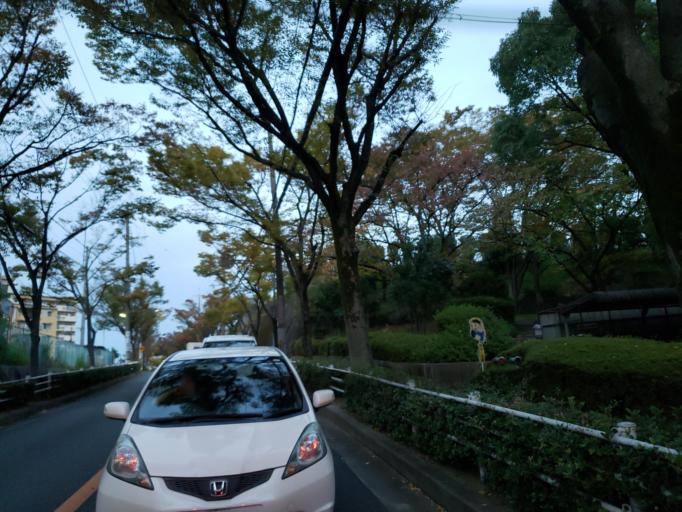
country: JP
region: Osaka
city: Suita
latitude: 34.7916
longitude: 135.5268
